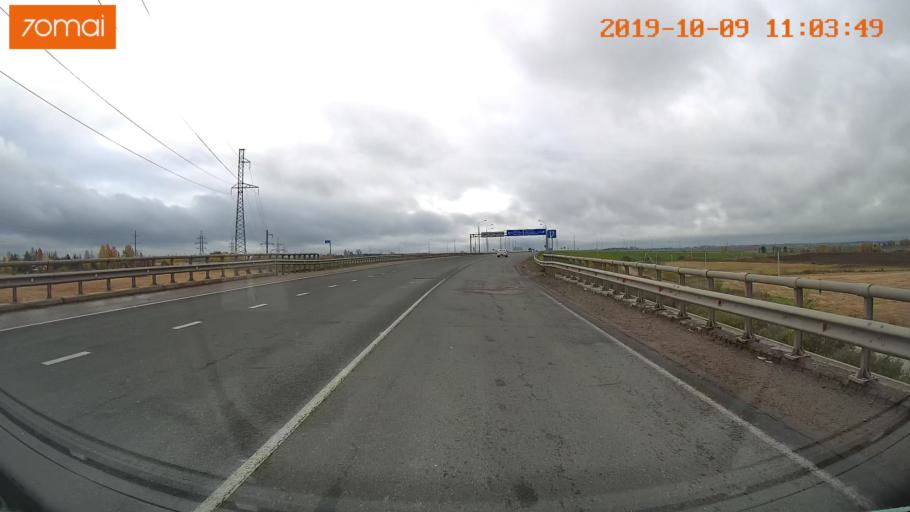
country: RU
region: Vologda
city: Vologda
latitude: 59.2185
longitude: 39.7739
